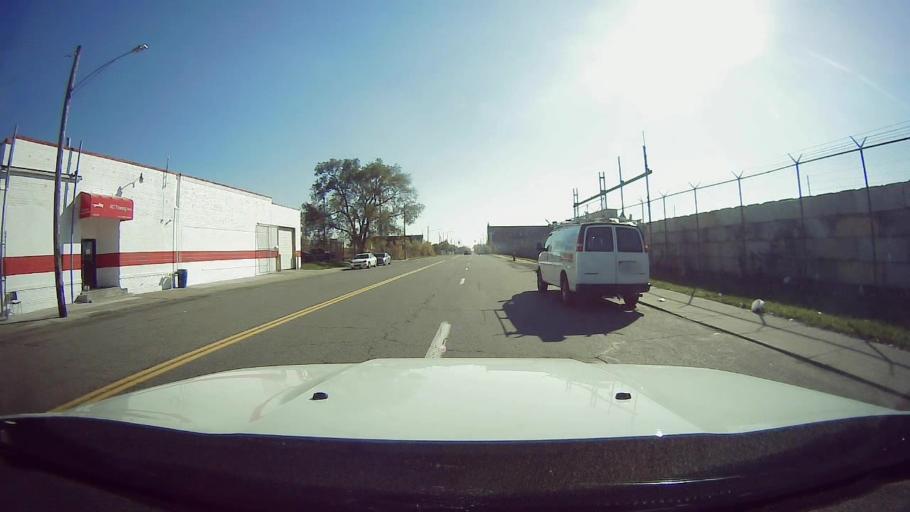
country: US
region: Michigan
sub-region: Wayne County
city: Detroit
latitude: 42.3512
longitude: -83.0878
